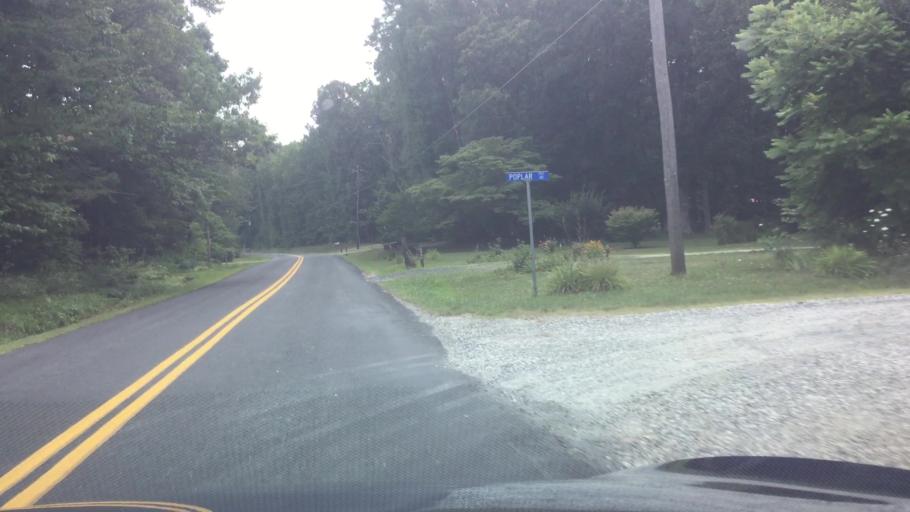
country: US
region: Virginia
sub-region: Appomattox County
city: Appomattox
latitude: 37.2897
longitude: -78.8518
